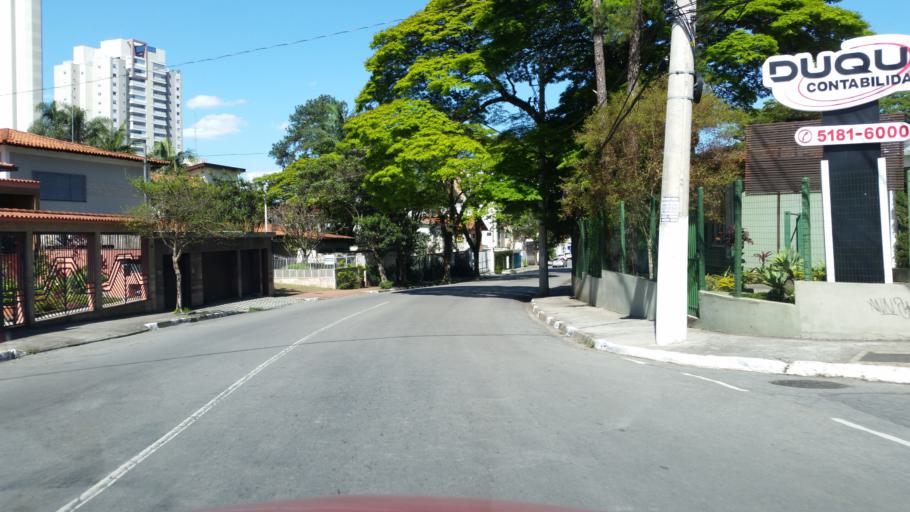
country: BR
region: Sao Paulo
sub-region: Taboao Da Serra
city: Taboao da Serra
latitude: -23.6344
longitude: -46.7035
